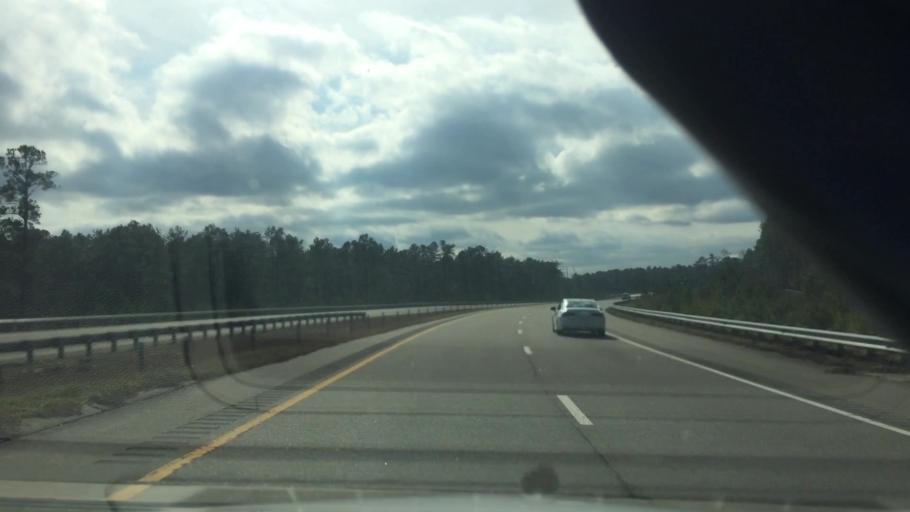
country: US
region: North Carolina
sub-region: Brunswick County
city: Leland
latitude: 34.2077
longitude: -78.0779
